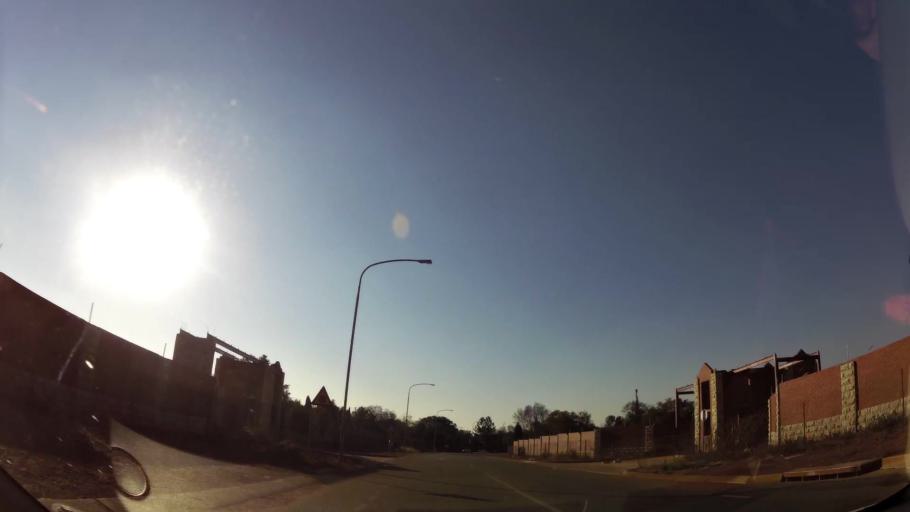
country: ZA
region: Gauteng
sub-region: City of Tshwane Metropolitan Municipality
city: Centurion
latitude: -25.8501
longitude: 28.1576
